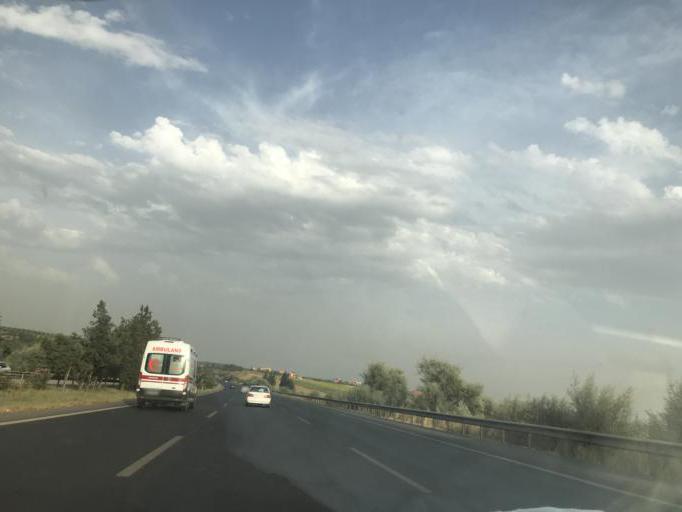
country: TR
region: Adana
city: Yakapinar
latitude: 37.0071
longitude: 35.5141
